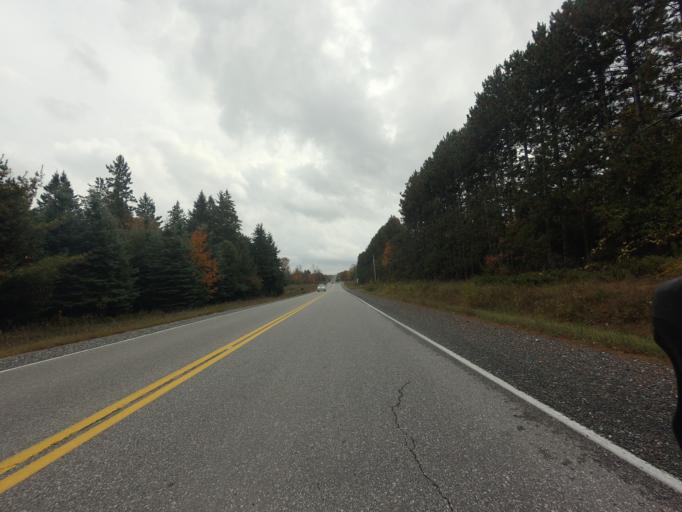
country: CA
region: Ontario
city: Perth
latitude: 45.0959
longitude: -76.4630
